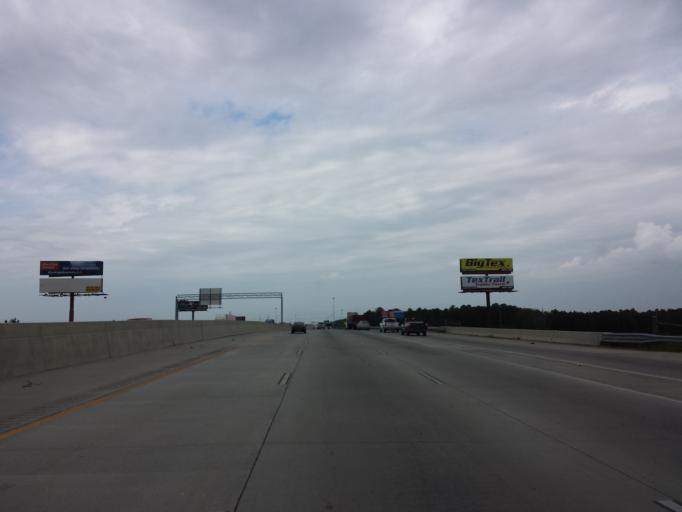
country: US
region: Georgia
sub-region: Crisp County
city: Cordele
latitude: 31.9627
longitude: -83.7519
